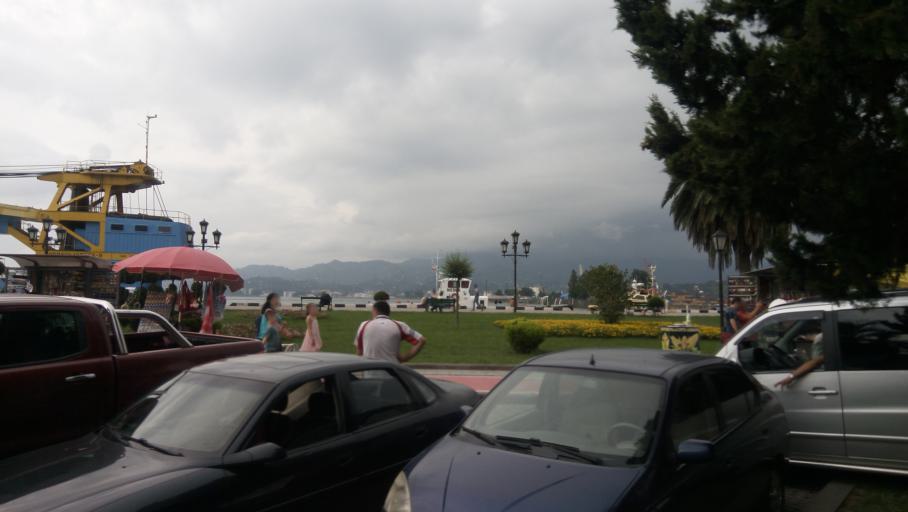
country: GE
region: Ajaria
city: Batumi
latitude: 41.6495
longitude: 41.6448
